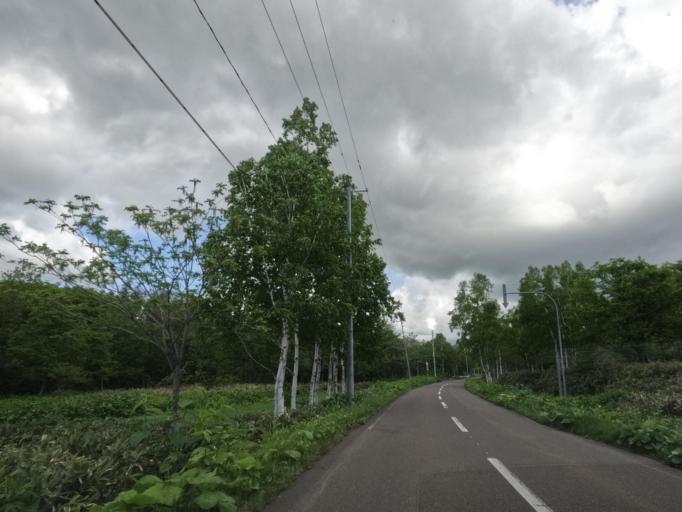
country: JP
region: Hokkaido
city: Tobetsu
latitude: 43.4577
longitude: 141.5923
